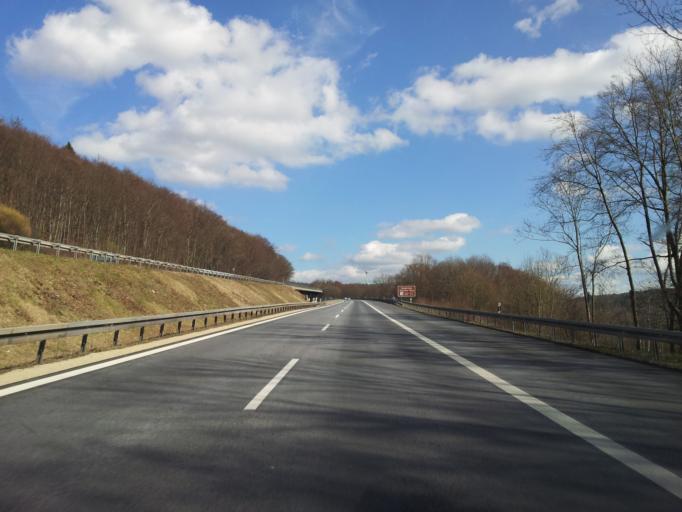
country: DE
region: Bavaria
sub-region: Upper Franconia
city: Schesslitz
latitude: 49.9837
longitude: 11.0828
